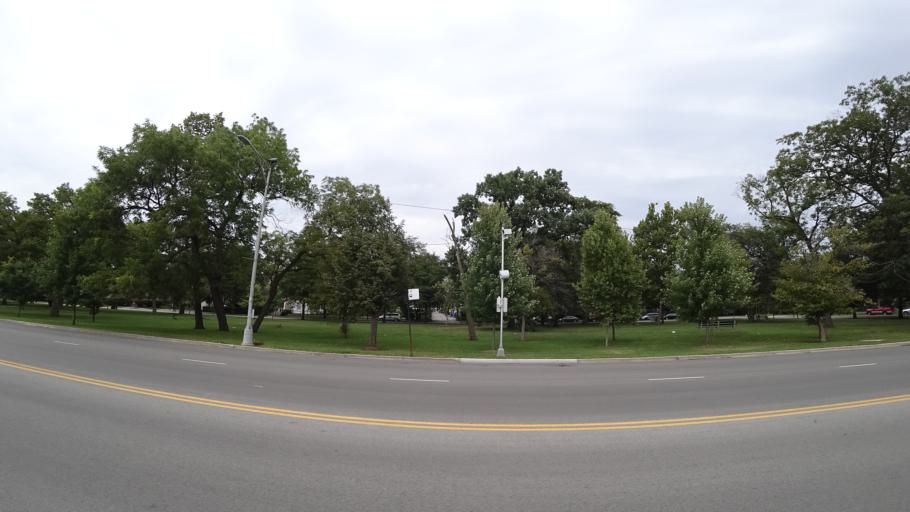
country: US
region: Illinois
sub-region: Cook County
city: Oak Park
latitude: 41.8771
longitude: -87.7706
